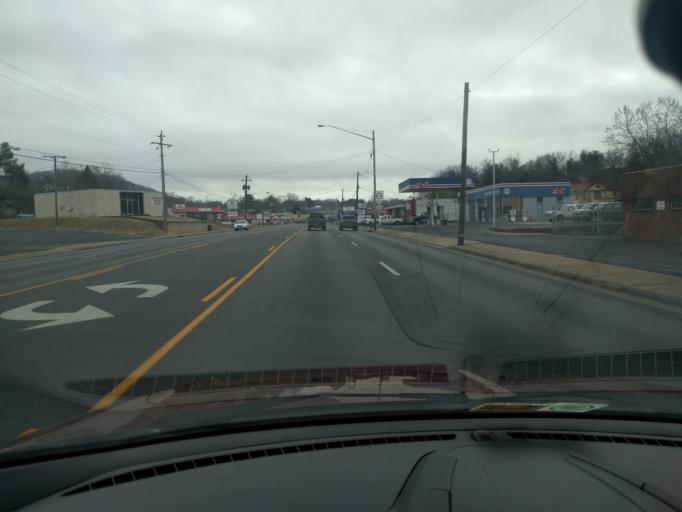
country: US
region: Virginia
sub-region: City of Staunton
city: Staunton
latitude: 38.1362
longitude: -79.0663
